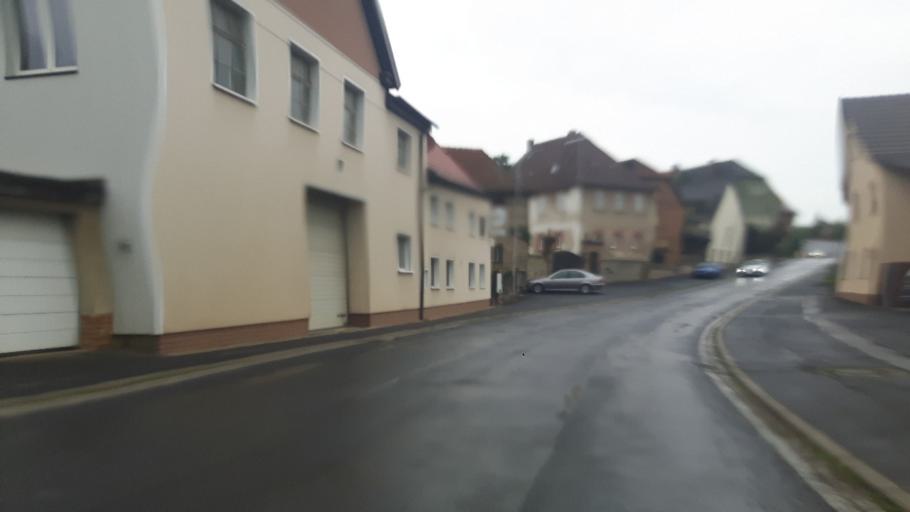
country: DE
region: Bavaria
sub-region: Regierungsbezirk Unterfranken
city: Schwanfeld
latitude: 49.9208
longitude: 10.1359
